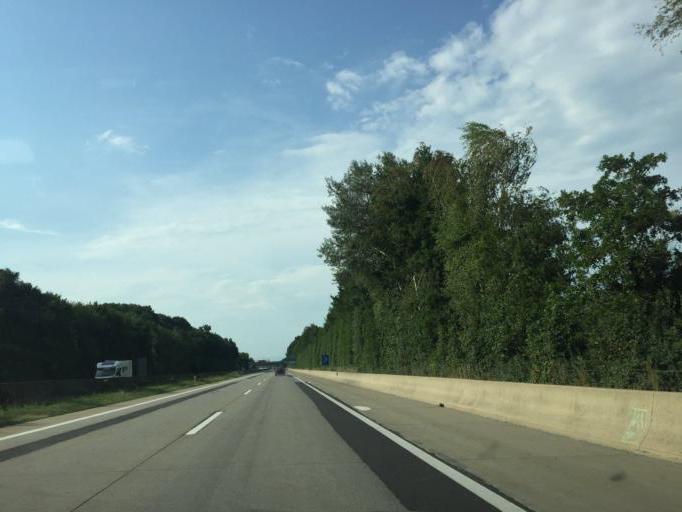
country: AT
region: Styria
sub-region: Politischer Bezirk Leibnitz
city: Gabersdorf
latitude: 46.7991
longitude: 15.5711
